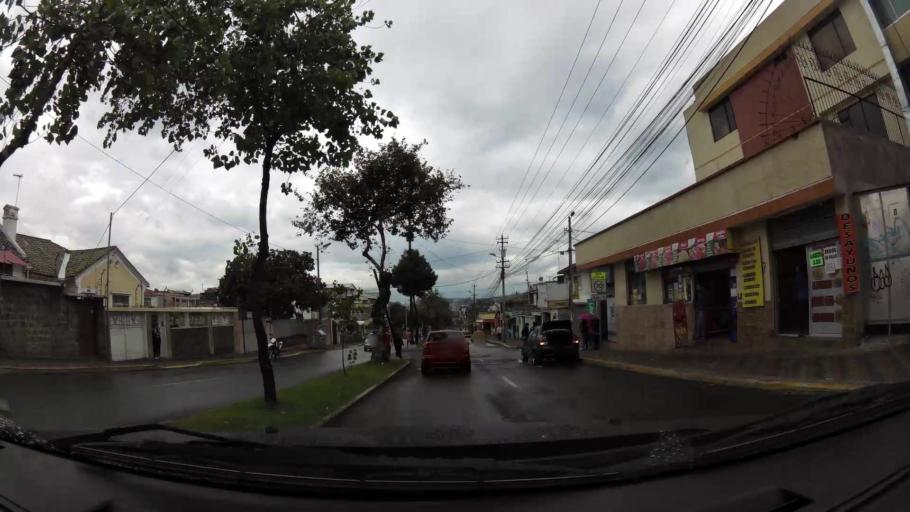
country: EC
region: Pichincha
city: Quito
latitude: -0.1961
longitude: -78.5045
